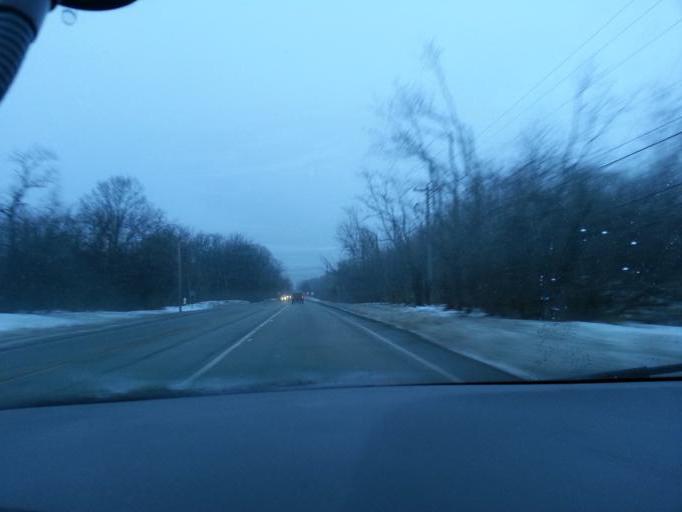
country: US
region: Illinois
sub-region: Kane County
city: Carpentersville
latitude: 42.1319
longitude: -88.2263
